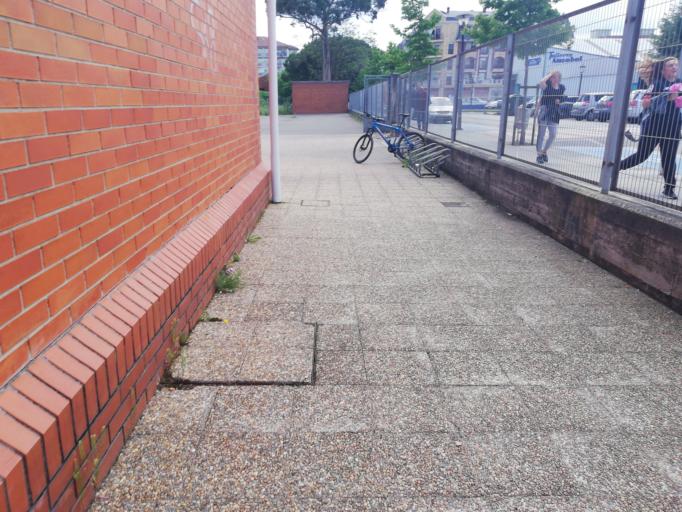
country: ES
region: Cantabria
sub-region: Provincia de Cantabria
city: Colindres
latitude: 43.3971
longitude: -3.4575
